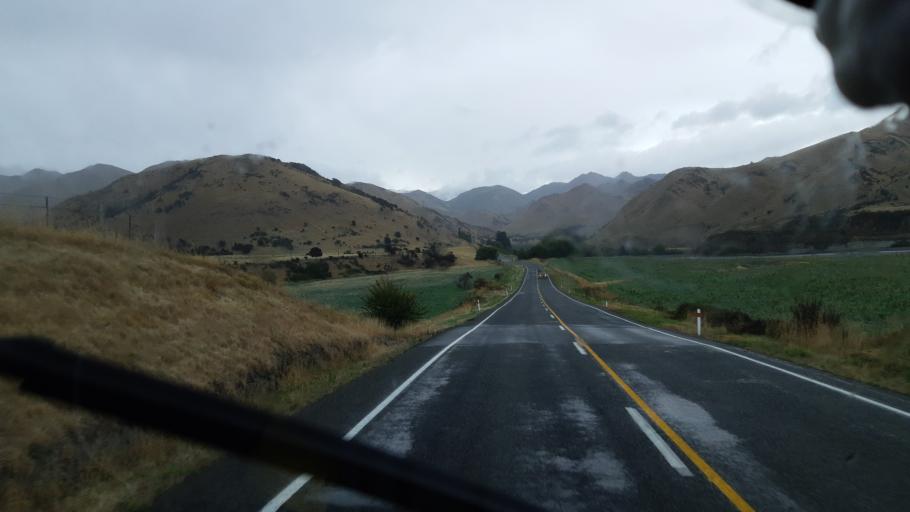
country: NZ
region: Canterbury
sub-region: Hurunui District
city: Amberley
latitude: -42.6751
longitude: 172.7817
